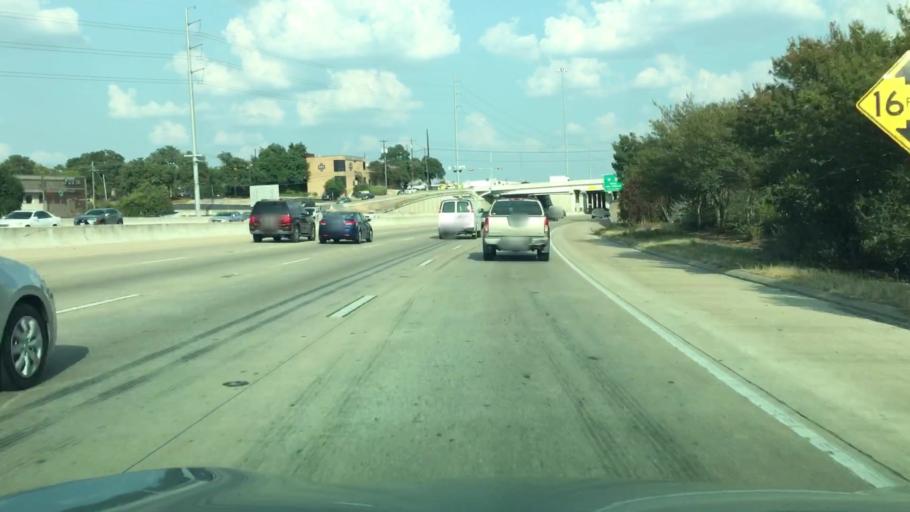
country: US
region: Texas
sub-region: Travis County
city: Austin
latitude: 30.2274
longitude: -97.7720
